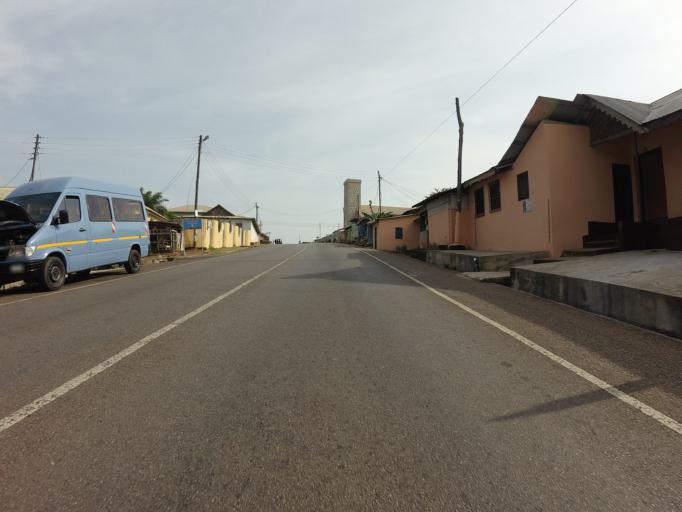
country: GH
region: Eastern
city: Aburi
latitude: 5.8887
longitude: -0.1543
